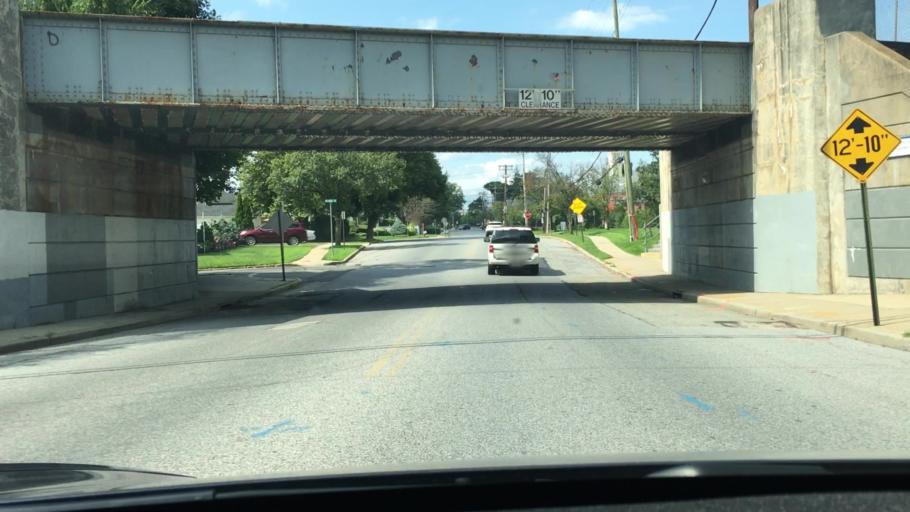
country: US
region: New York
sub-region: Nassau County
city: Carle Place
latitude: 40.7485
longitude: -73.6057
